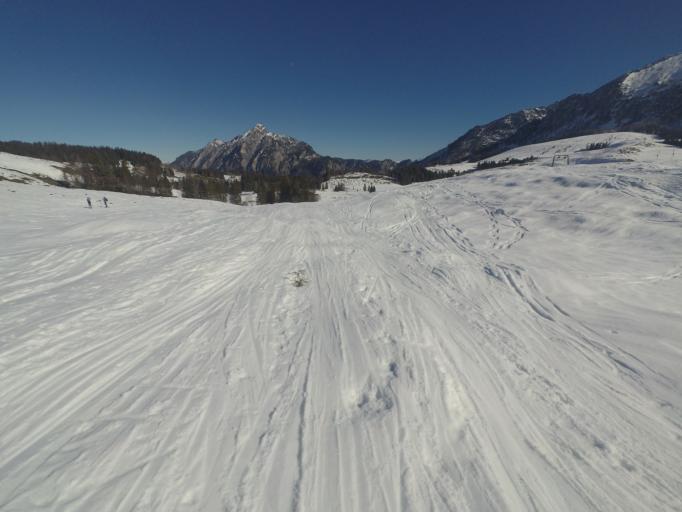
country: AT
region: Salzburg
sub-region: Politischer Bezirk Salzburg-Umgebung
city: Strobl
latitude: 47.6496
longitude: 13.4241
